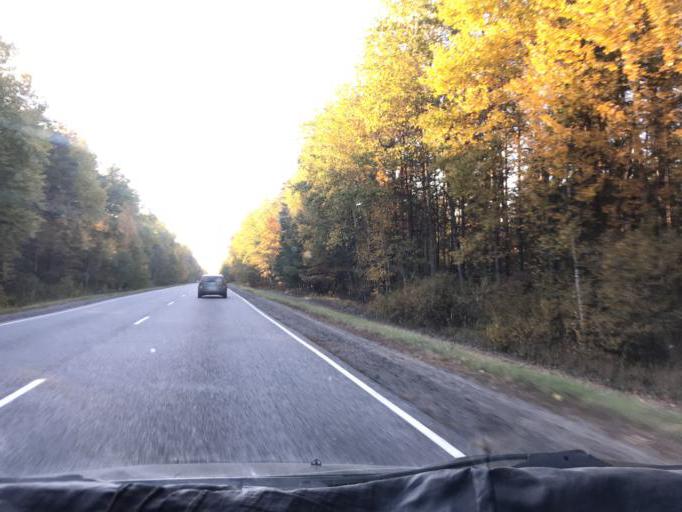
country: BY
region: Gomel
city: Zhytkavichy
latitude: 52.2733
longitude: 28.1091
